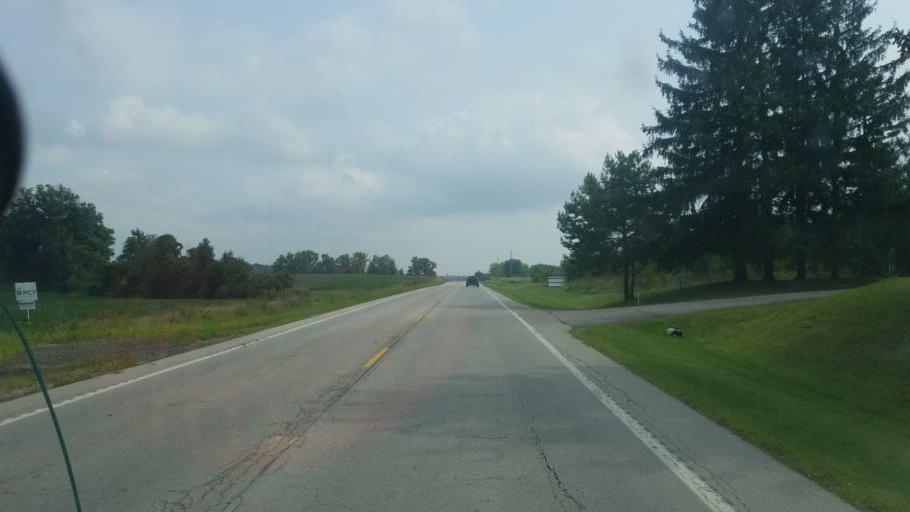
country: US
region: Ohio
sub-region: Huron County
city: Greenwich
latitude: 41.0881
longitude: -82.4766
